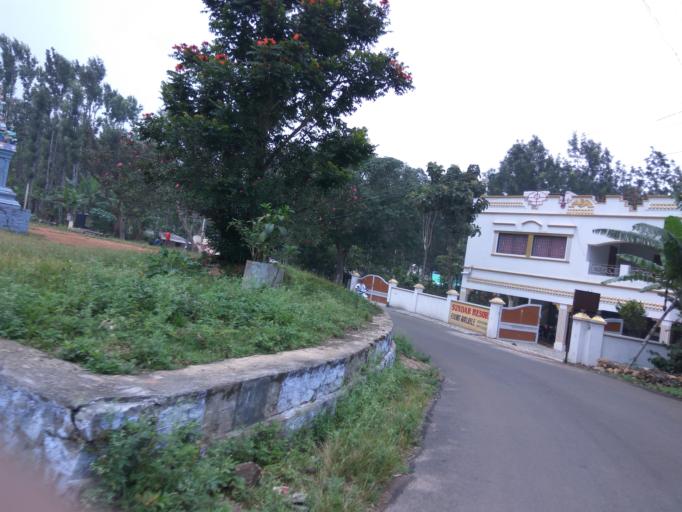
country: IN
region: Tamil Nadu
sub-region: Salem
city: Salem
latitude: 11.7694
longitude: 78.2364
